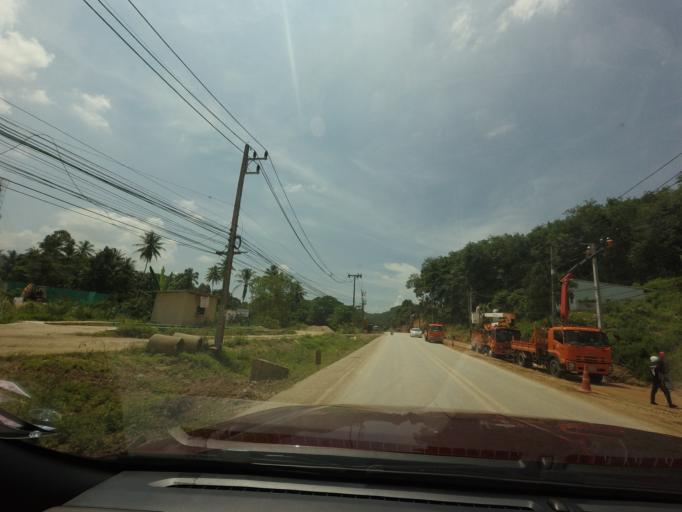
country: TH
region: Yala
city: Betong
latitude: 5.8055
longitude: 101.0747
